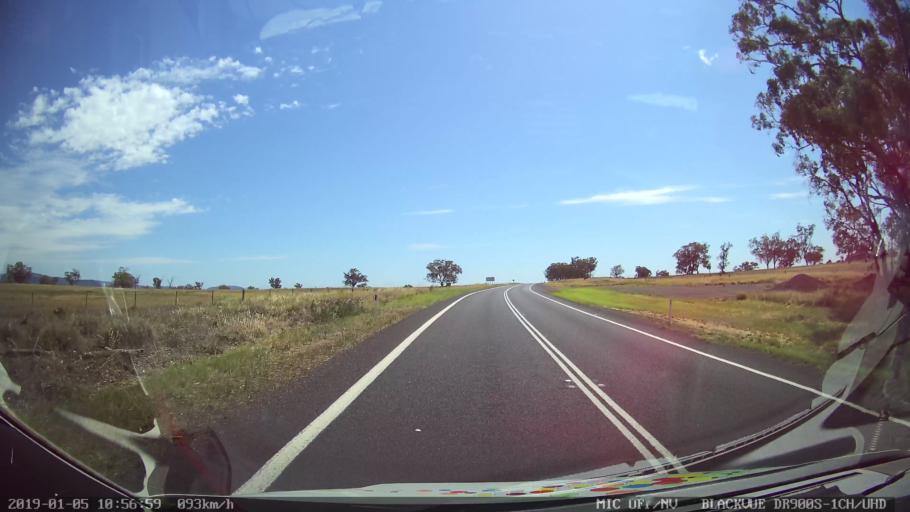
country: AU
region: New South Wales
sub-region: Warrumbungle Shire
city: Coonabarabran
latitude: -31.4353
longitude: 149.1640
